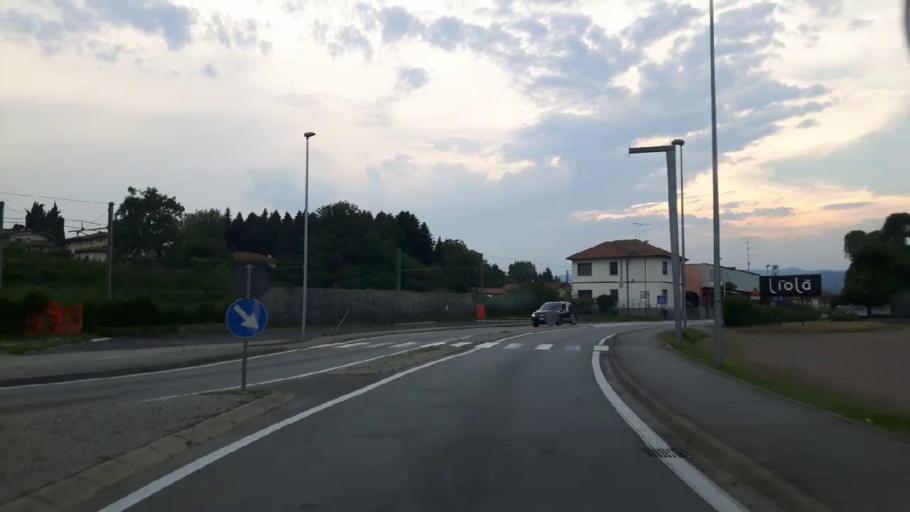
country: IT
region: Piedmont
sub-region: Provincia di Novara
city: Dormelletto
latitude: 45.7349
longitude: 8.5739
